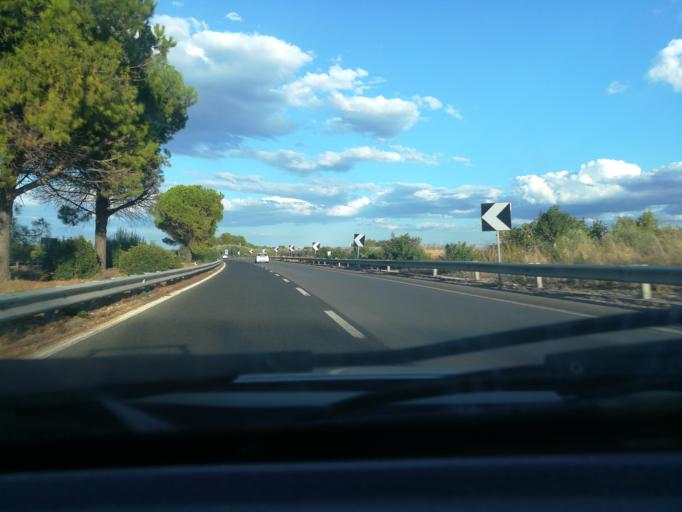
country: IT
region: Apulia
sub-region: Provincia di Bari
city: Mola di Bari
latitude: 41.0481
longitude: 17.0812
